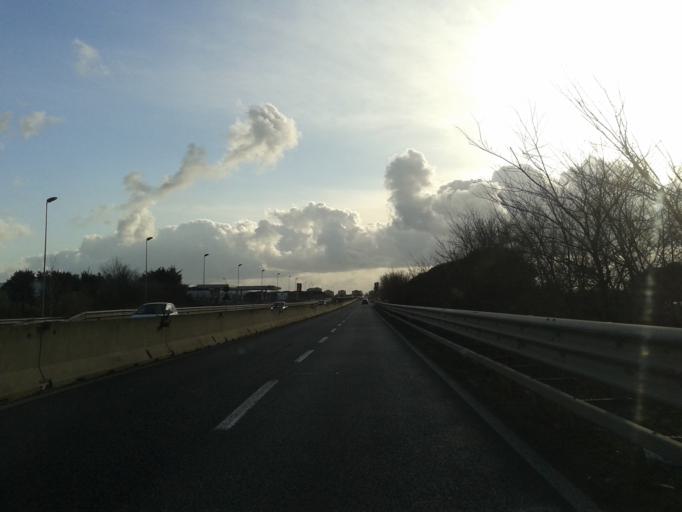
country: IT
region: Tuscany
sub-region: Provincia di Livorno
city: Livorno
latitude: 43.5532
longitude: 10.3435
